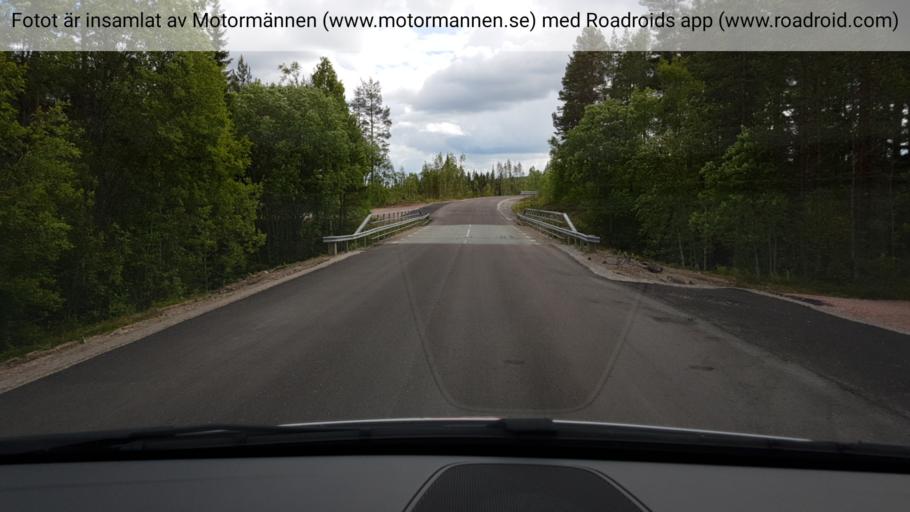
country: SE
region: Jaemtland
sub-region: Harjedalens Kommun
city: Sveg
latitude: 61.6977
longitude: 14.1861
